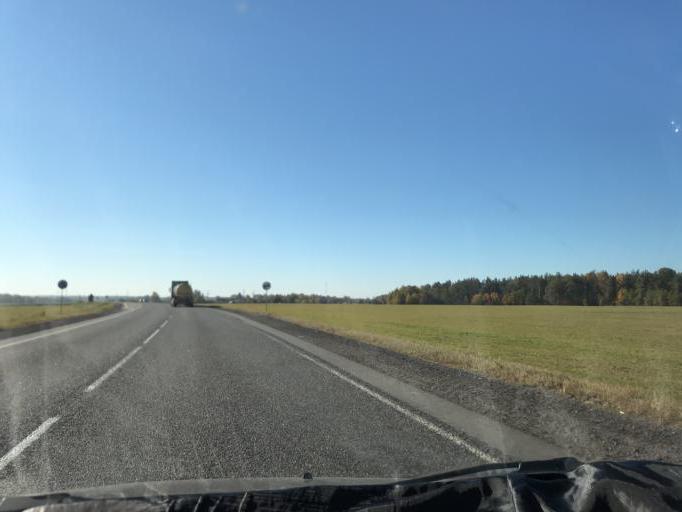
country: BY
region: Mogilev
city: Babruysk
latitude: 53.1941
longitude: 29.0539
